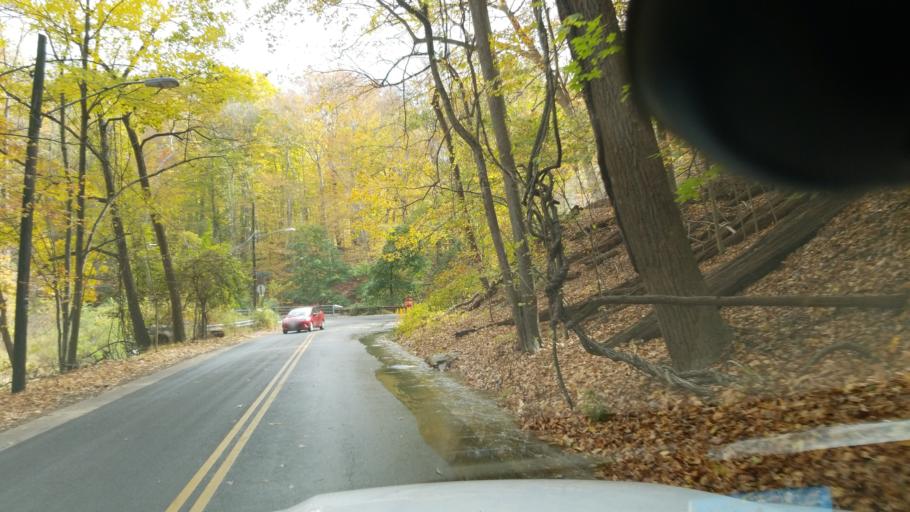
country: US
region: Maryland
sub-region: Montgomery County
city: Chevy Chase
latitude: 38.9574
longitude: -77.0589
